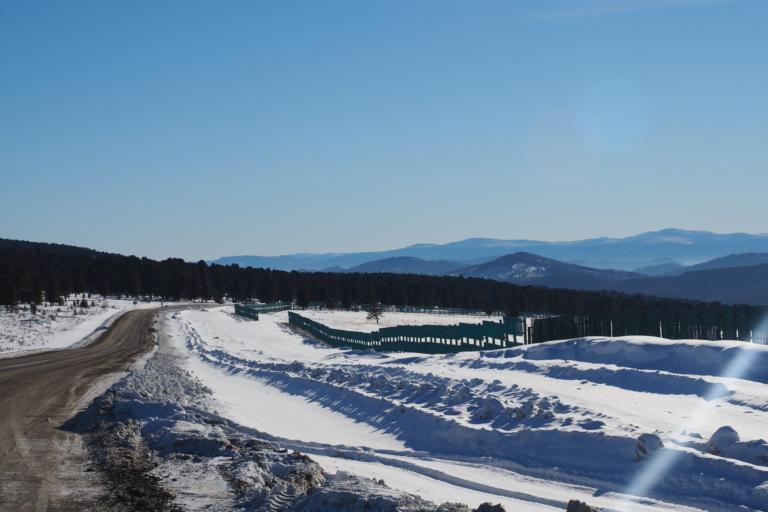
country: RU
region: Altay
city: Shebalino
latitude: 51.0445
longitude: 85.6053
